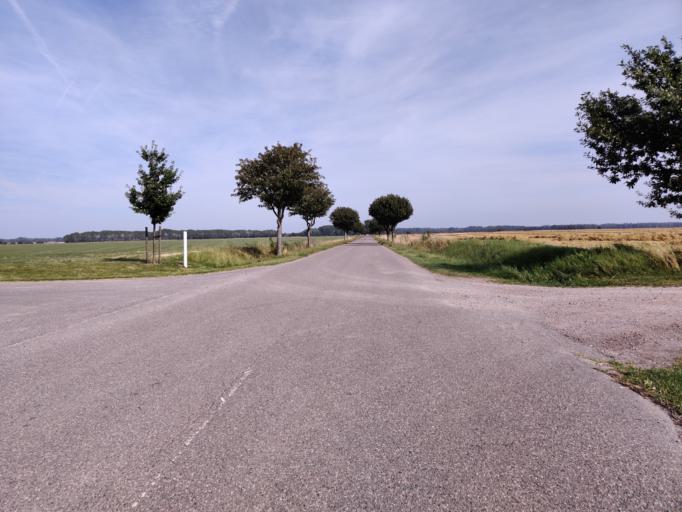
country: DK
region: Zealand
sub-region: Guldborgsund Kommune
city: Nykobing Falster
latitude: 54.6350
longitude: 11.9114
